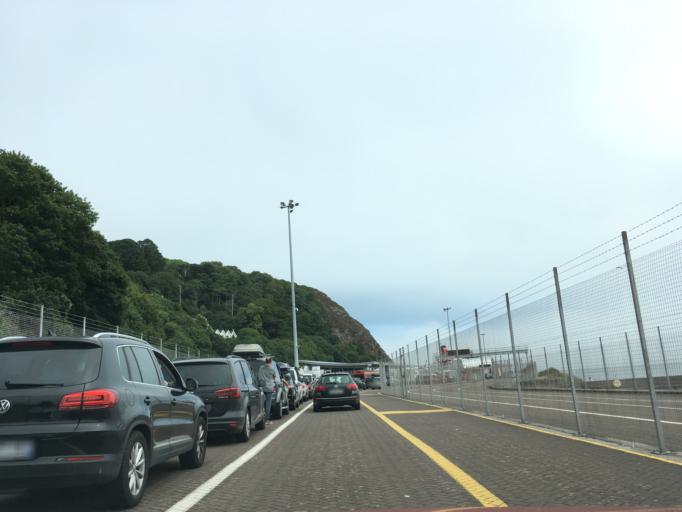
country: GB
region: Wales
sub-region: Pembrokeshire
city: Goodwick
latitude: 52.0066
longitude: -4.9910
